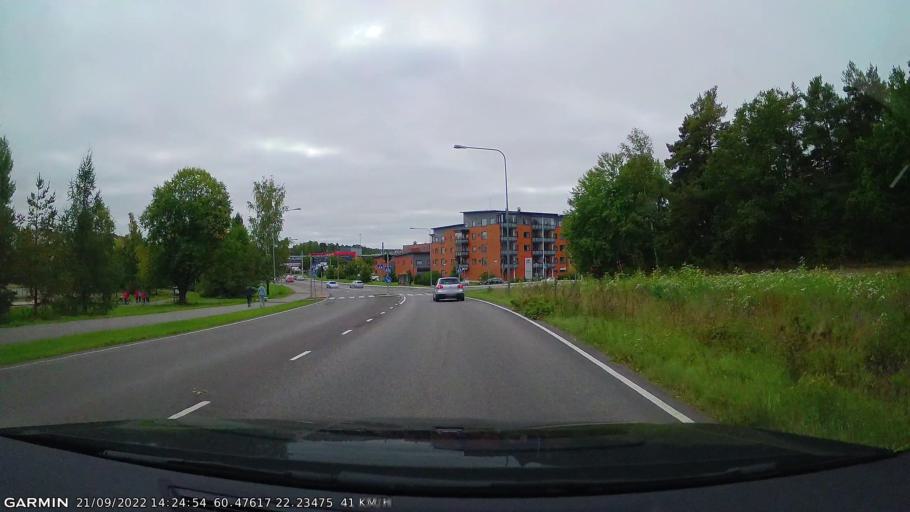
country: FI
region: Varsinais-Suomi
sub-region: Turku
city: Turku
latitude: 60.4761
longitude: 22.2346
